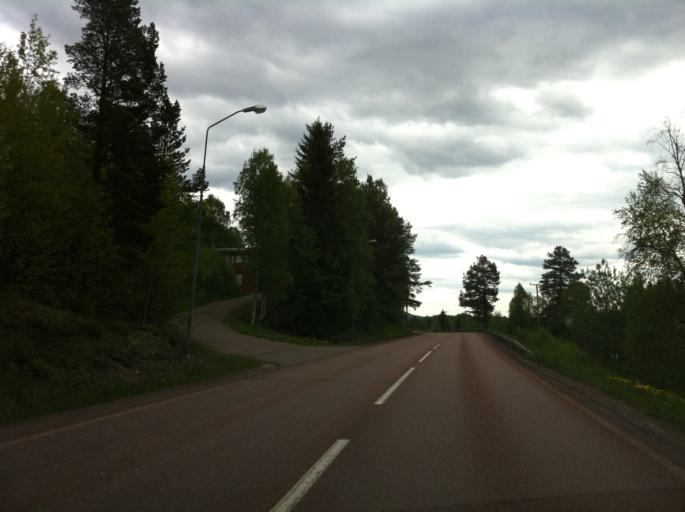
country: SE
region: Dalarna
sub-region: Malung-Saelens kommun
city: Malung
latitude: 61.0904
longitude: 13.3199
